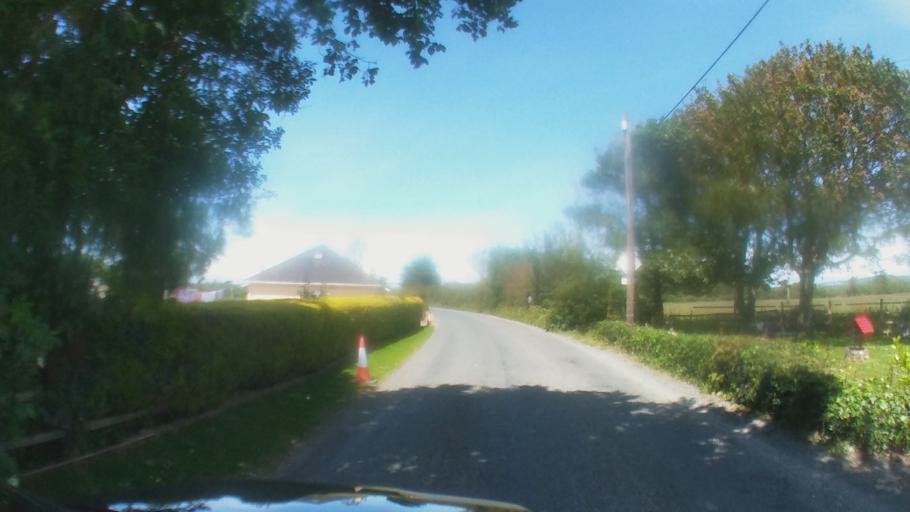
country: IE
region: Leinster
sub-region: Loch Garman
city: Loch Garman
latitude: 52.2341
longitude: -6.5663
